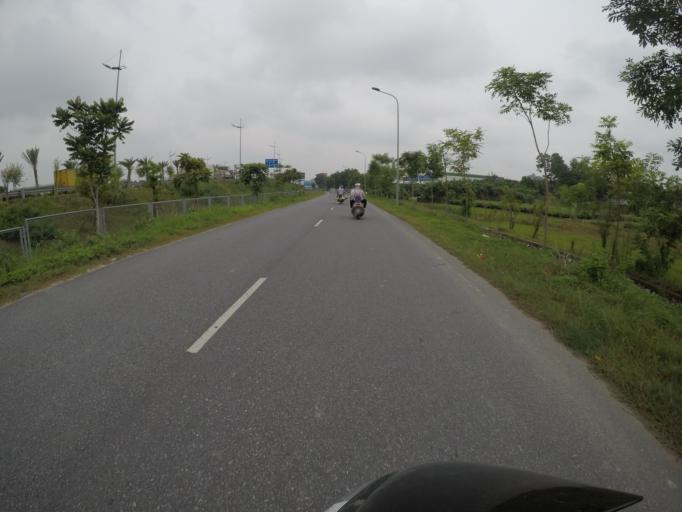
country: VN
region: Ha Noi
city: Dong Anh
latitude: 21.1956
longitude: 105.8356
